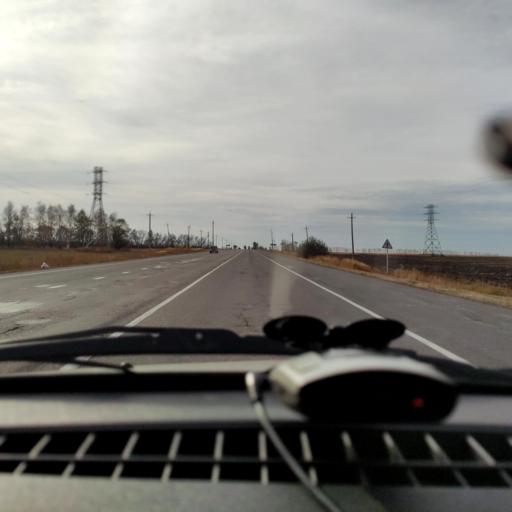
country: RU
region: Voronezj
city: Strelitsa
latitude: 51.5471
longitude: 38.9715
